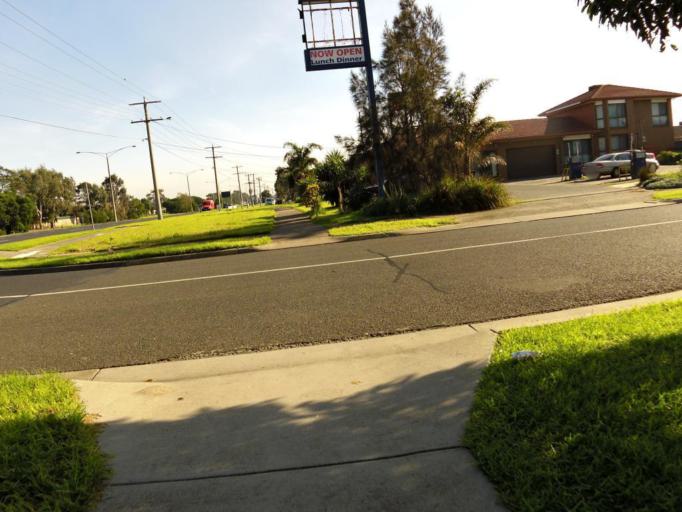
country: AU
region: Victoria
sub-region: Kingston
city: Aspendale Gardens
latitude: -38.0178
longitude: 145.1142
